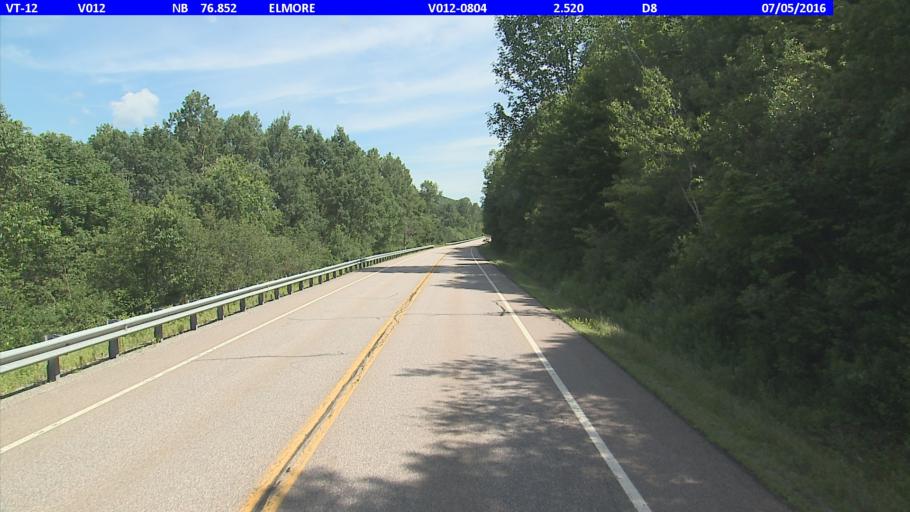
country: US
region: Vermont
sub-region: Lamoille County
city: Morrisville
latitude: 44.4832
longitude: -72.5270
